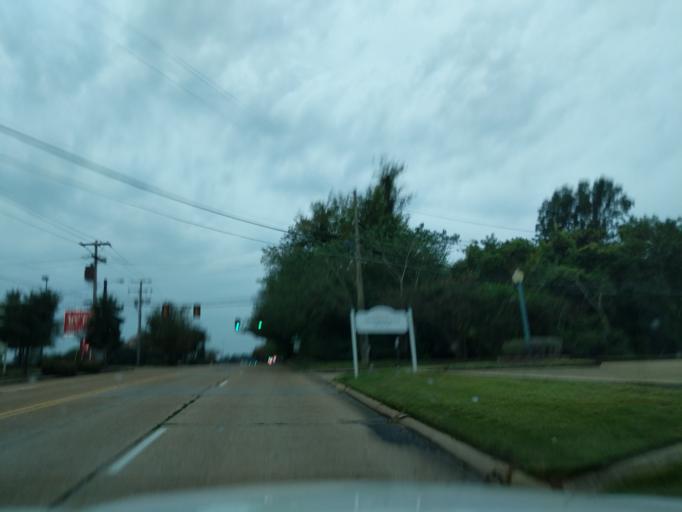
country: US
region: Mississippi
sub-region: Warren County
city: Vicksburg
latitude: 32.3171
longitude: -90.8976
